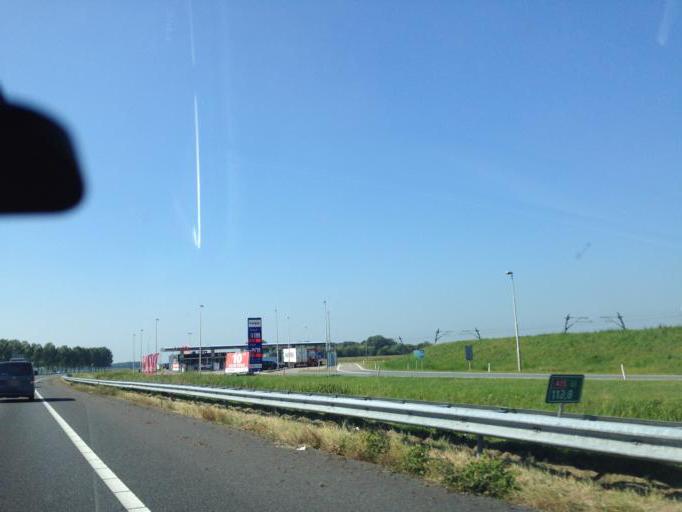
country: NL
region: Gelderland
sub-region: Gemeente Zaltbommel
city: Zaltbommel
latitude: 51.8490
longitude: 5.1942
